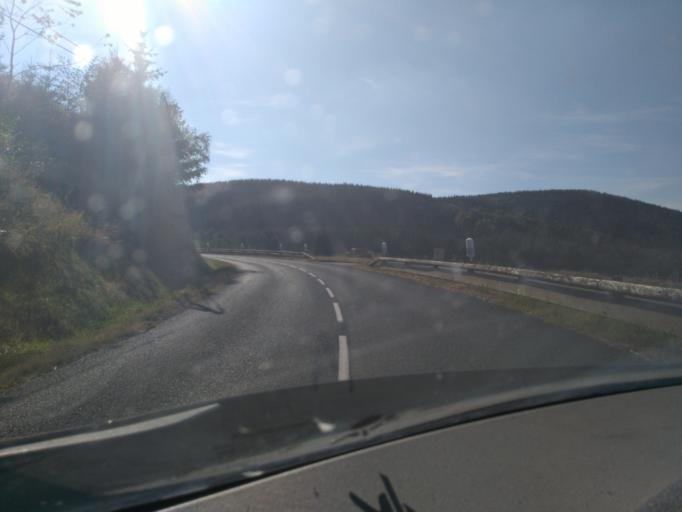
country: FR
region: Rhone-Alpes
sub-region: Departement de la Loire
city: Violay
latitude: 45.8489
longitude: 4.4031
